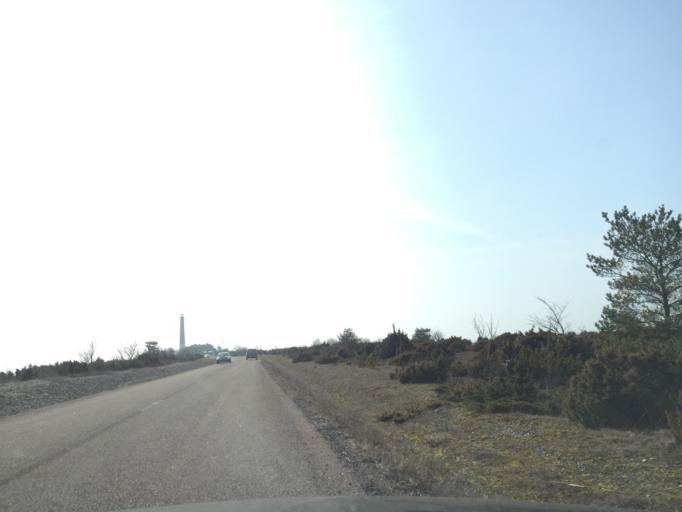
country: LV
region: Dundaga
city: Dundaga
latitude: 57.9159
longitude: 22.0611
